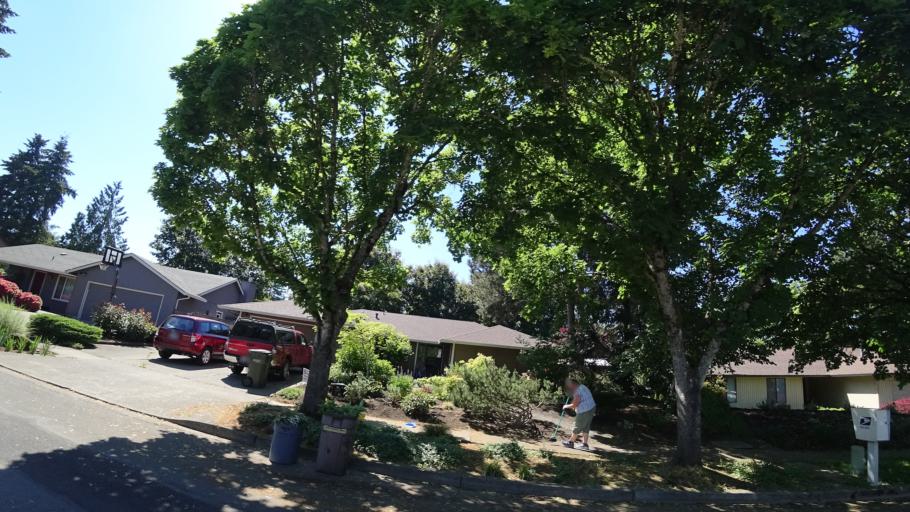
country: US
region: Oregon
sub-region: Washington County
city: Beaverton
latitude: 45.4527
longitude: -122.8003
